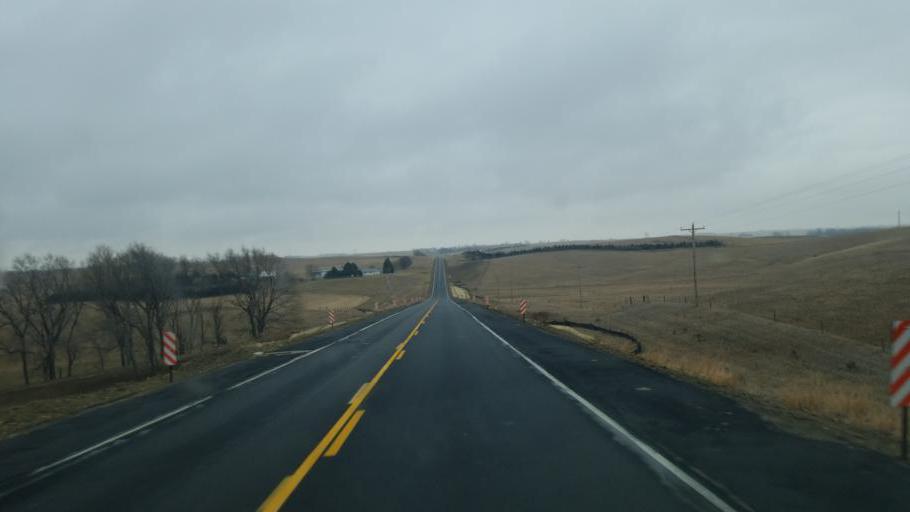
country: US
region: Nebraska
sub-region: Knox County
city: Center
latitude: 42.5971
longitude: -97.7763
